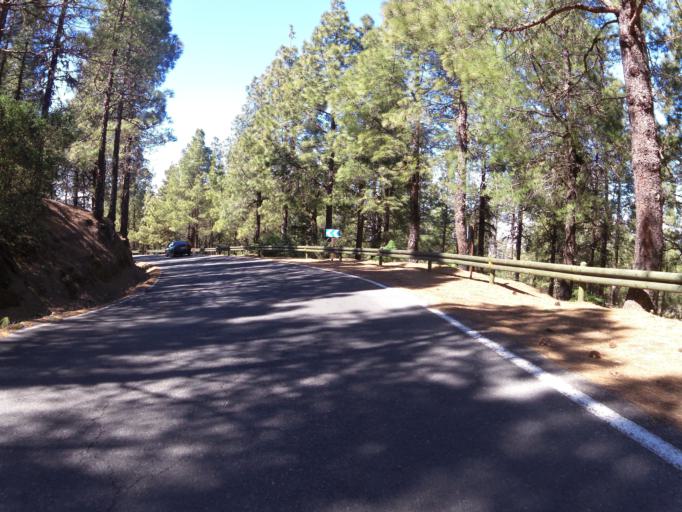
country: ES
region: Canary Islands
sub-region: Provincia de Las Palmas
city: Tejeda
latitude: 27.9855
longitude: -15.5789
